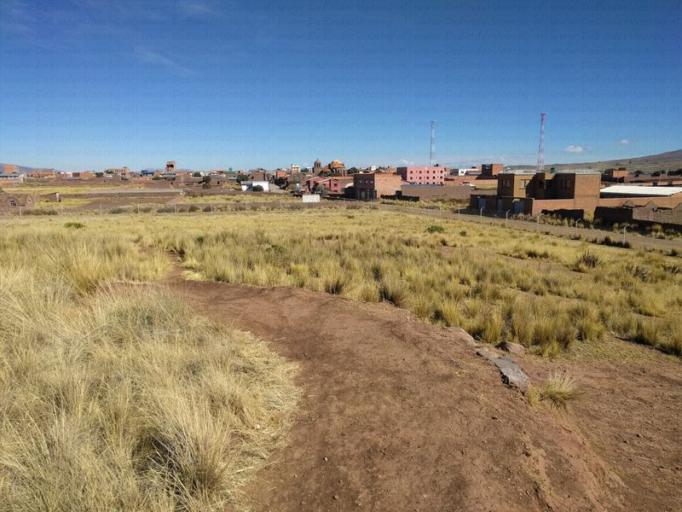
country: BO
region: La Paz
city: Tiahuanaco
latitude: -16.5536
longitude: -68.6761
